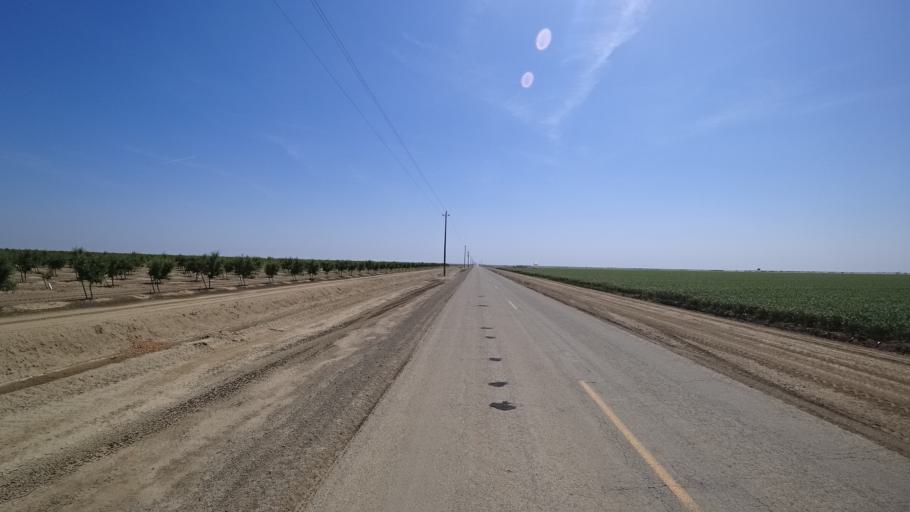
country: US
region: California
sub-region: Kings County
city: Kettleman City
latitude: 36.0943
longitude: -119.9799
